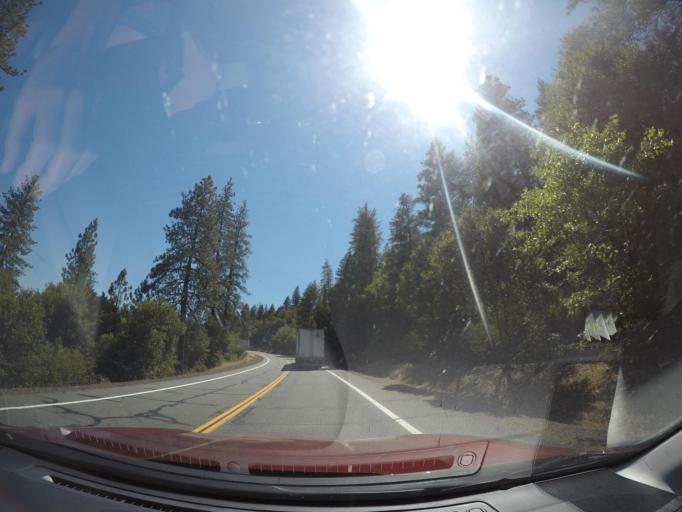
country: US
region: California
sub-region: Shasta County
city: Bella Vista
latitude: 40.7110
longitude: -122.0895
